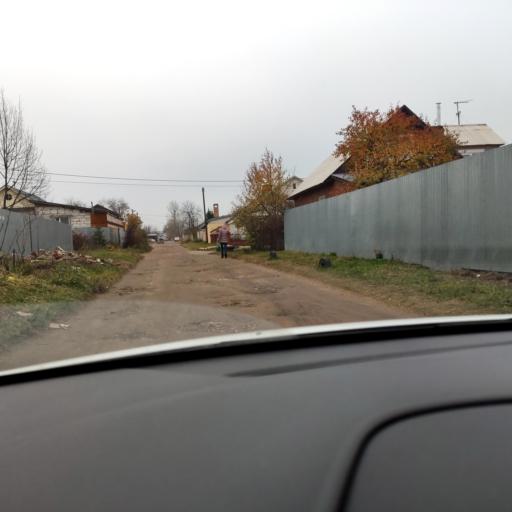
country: RU
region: Tatarstan
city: Vysokaya Gora
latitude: 55.8500
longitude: 49.2188
